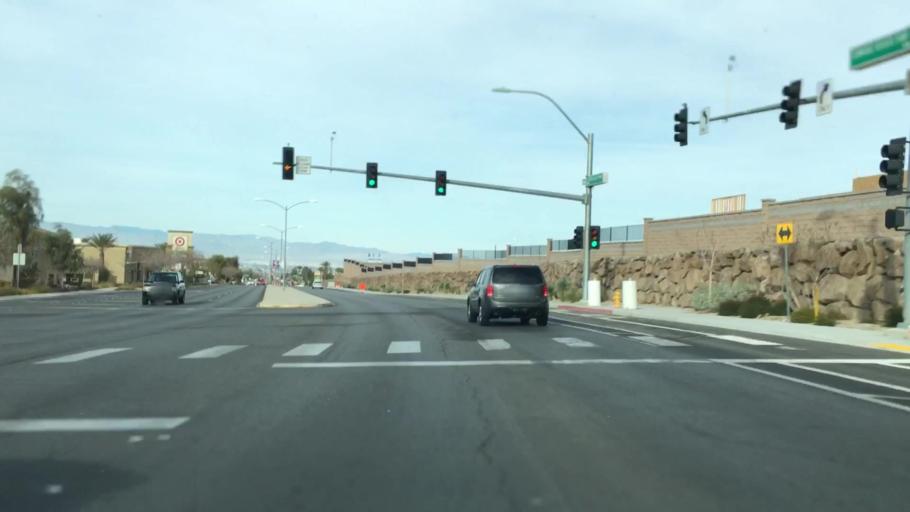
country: US
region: Nevada
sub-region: Clark County
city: Whitney
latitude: 36.0002
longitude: -115.0832
